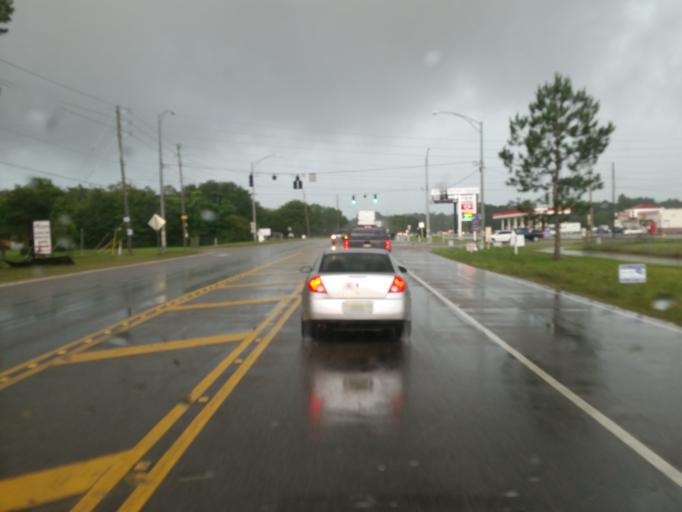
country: US
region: Alabama
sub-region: Mobile County
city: Chickasaw
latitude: 30.7848
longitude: -88.2773
